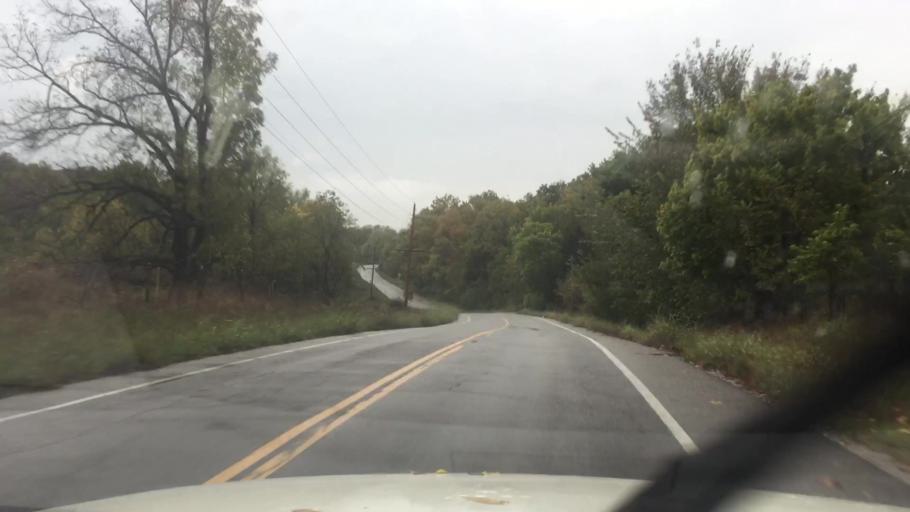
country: US
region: Missouri
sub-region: Boone County
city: Columbia
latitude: 38.8841
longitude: -92.4271
